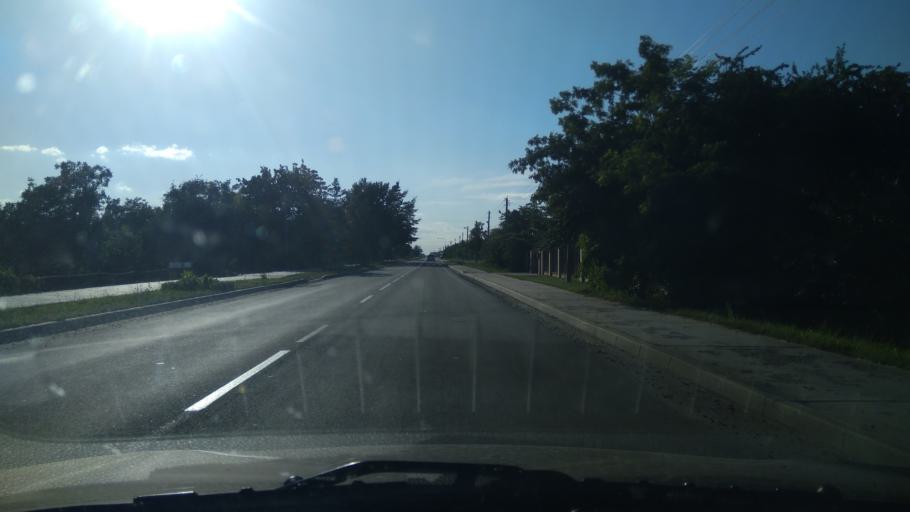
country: BY
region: Brest
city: Byaroza
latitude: 52.5423
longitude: 24.9714
